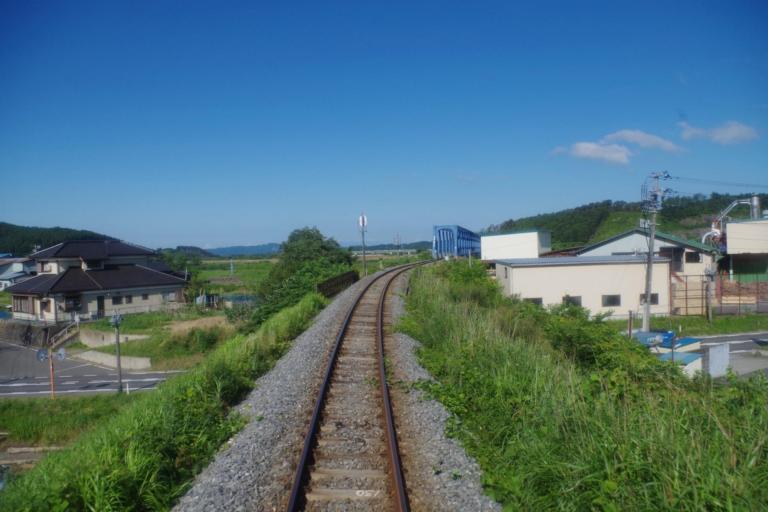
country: JP
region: Miyagi
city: Wakuya
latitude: 38.6091
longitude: 141.3016
